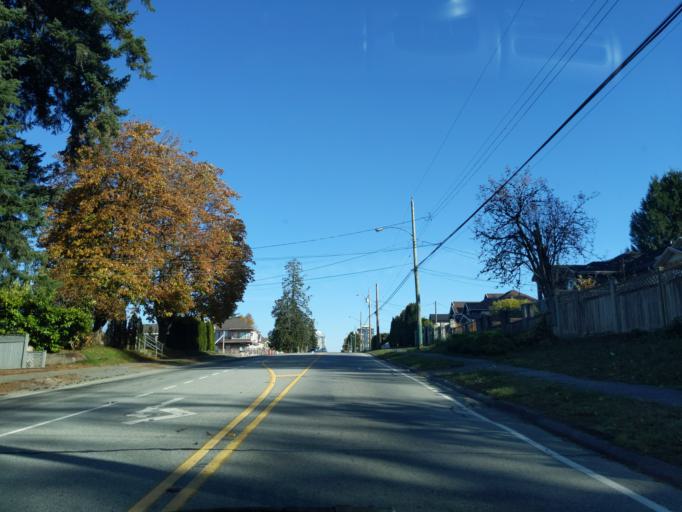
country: CA
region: British Columbia
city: New Westminster
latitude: 49.1990
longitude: -122.8643
